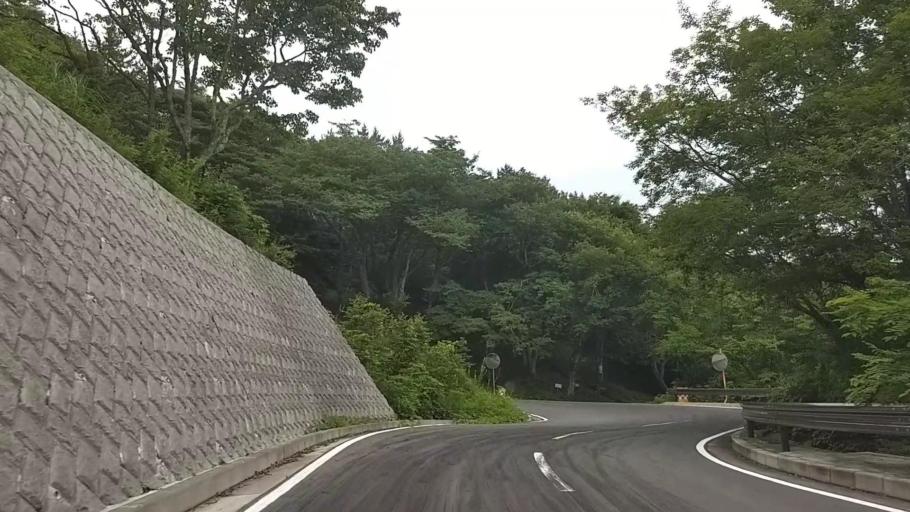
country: JP
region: Shizuoka
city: Gotemba
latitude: 35.3237
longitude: 139.0177
